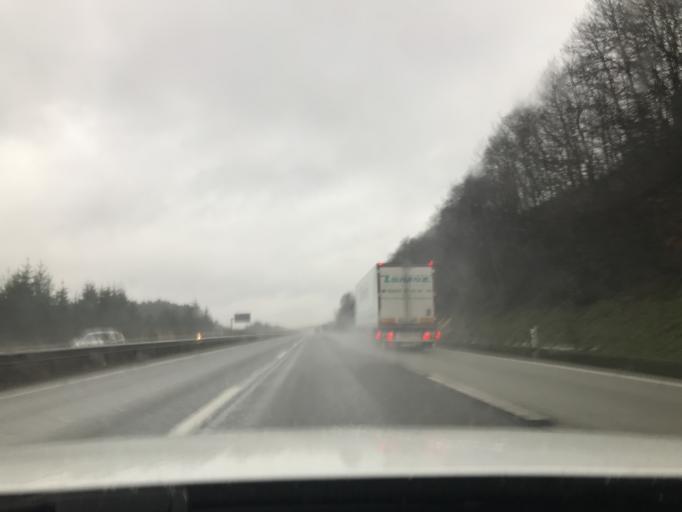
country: DE
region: Rheinland-Pfalz
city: Willroth
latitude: 50.5665
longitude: 7.5220
